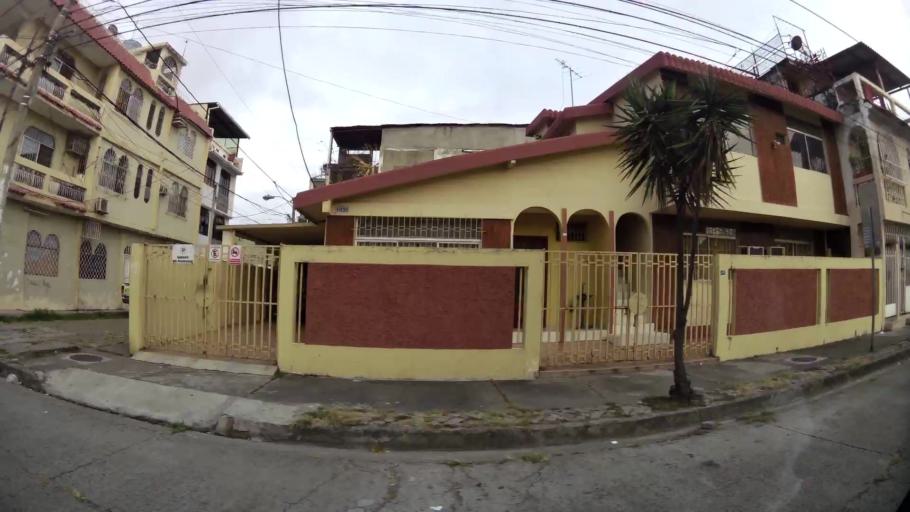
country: EC
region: Guayas
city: Eloy Alfaro
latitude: -2.1740
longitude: -79.8856
